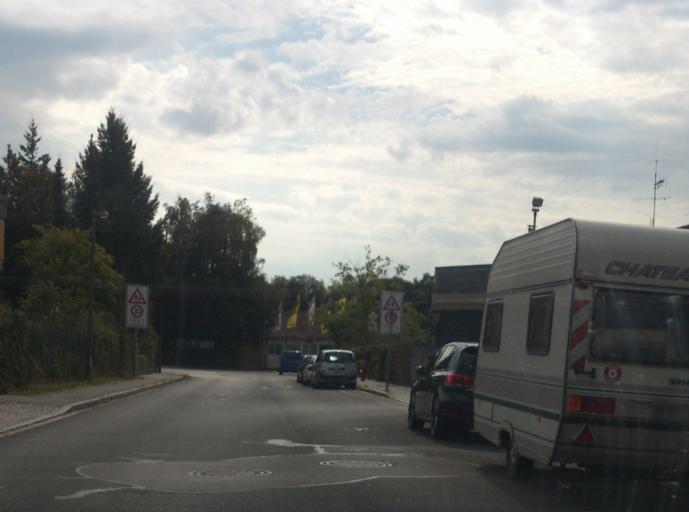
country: DE
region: Bavaria
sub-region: Regierungsbezirk Mittelfranken
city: Wetzendorf
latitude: 49.5170
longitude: 11.0360
